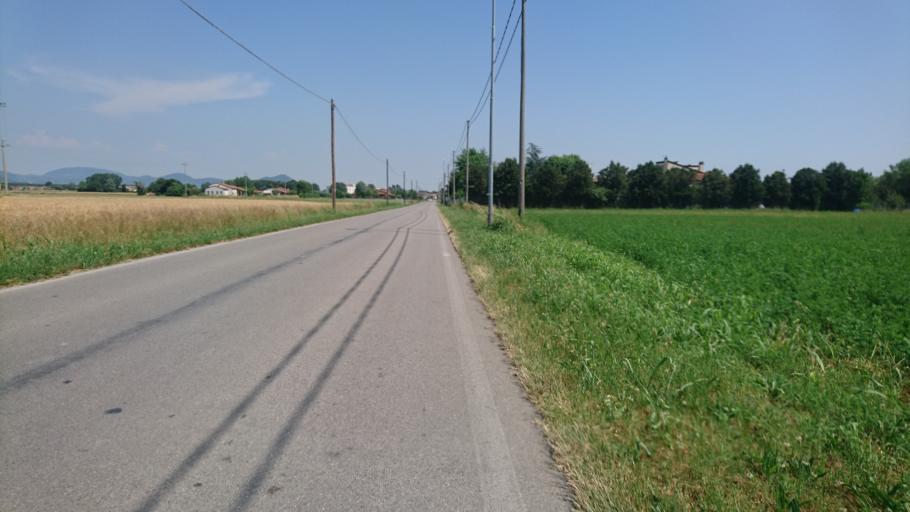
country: IT
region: Veneto
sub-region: Provincia di Padova
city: Solesino
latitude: 45.1656
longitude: 11.7368
